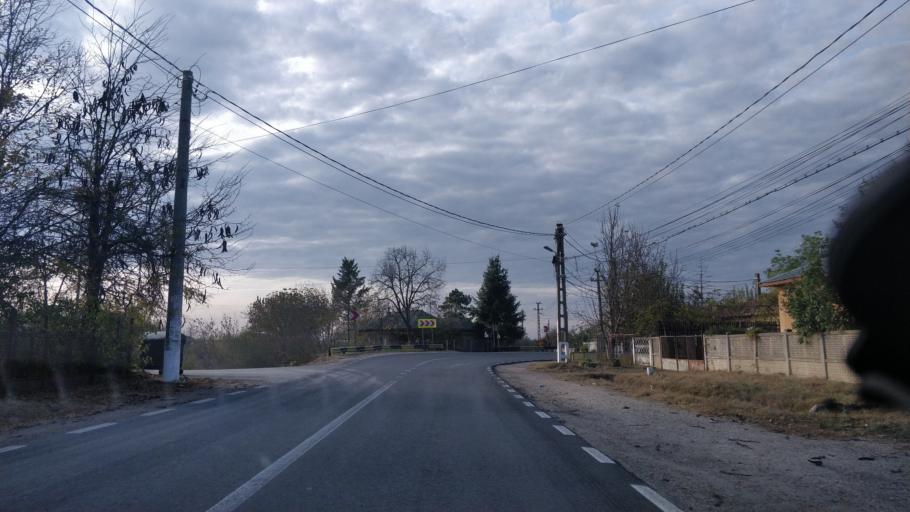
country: RO
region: Giurgiu
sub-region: Comuna Clejani
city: Clejani
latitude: 44.3431
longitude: 25.6716
